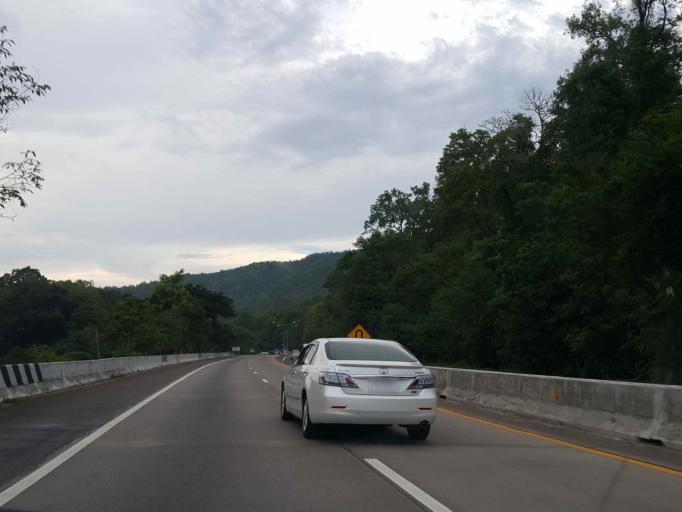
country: TH
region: Lampang
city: Hang Chat
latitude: 18.3680
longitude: 99.2365
